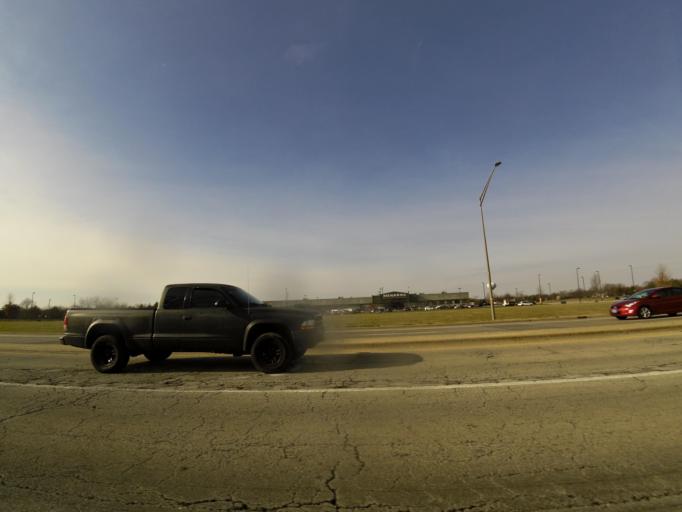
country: US
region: Illinois
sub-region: Macon County
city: Forsyth
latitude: 39.9293
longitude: -88.9556
